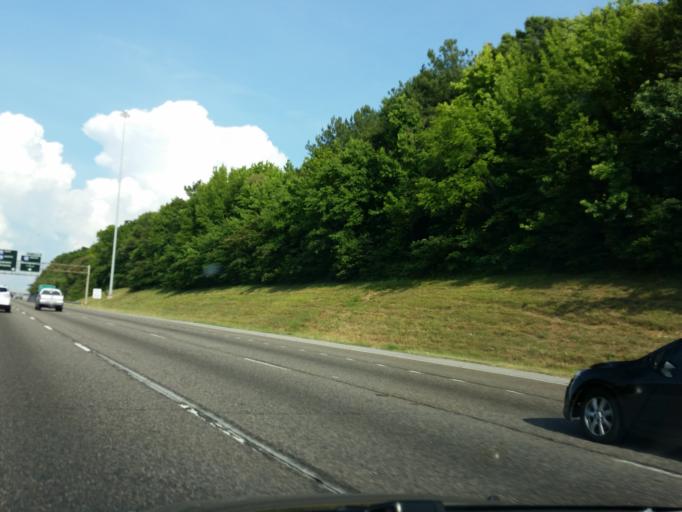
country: US
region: Alabama
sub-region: Jefferson County
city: Birmingham
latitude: 33.5209
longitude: -86.8441
